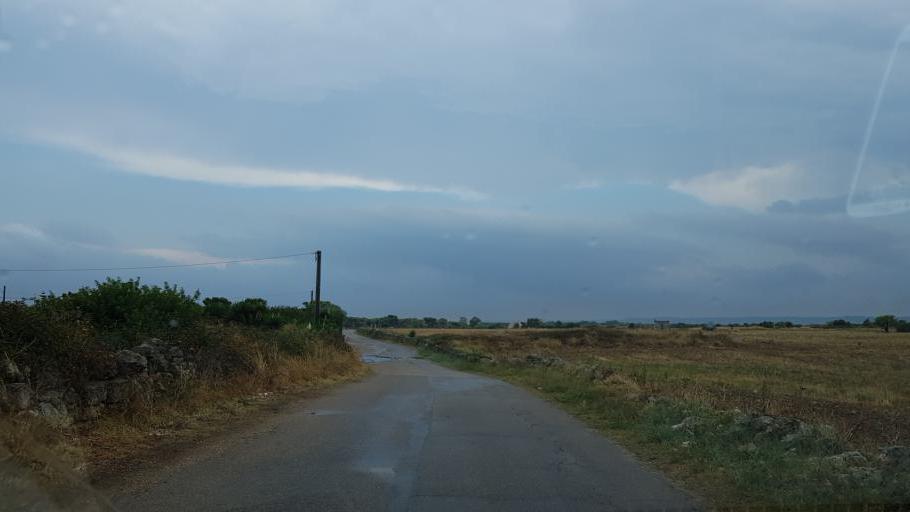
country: IT
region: Apulia
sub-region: Provincia di Bari
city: Monopoli
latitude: 40.9317
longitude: 17.3244
